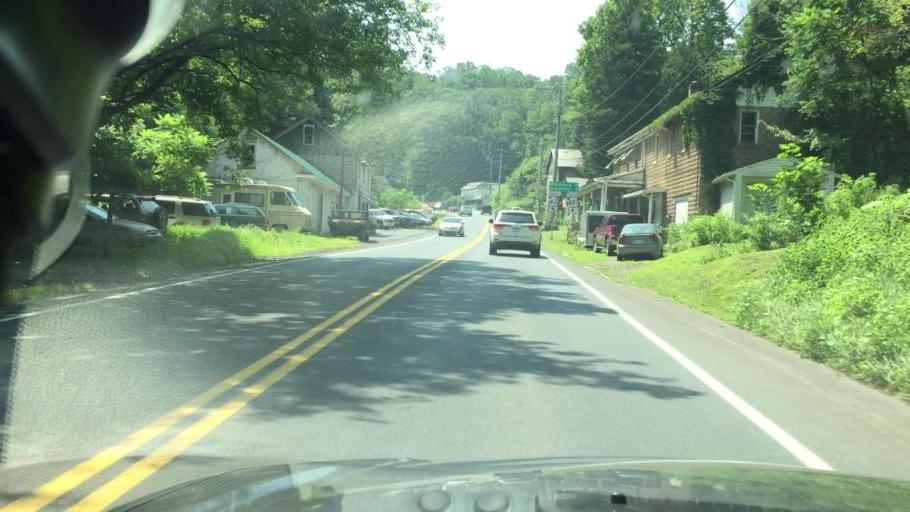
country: US
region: Pennsylvania
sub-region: Columbia County
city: Catawissa
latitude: 40.9445
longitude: -76.4569
